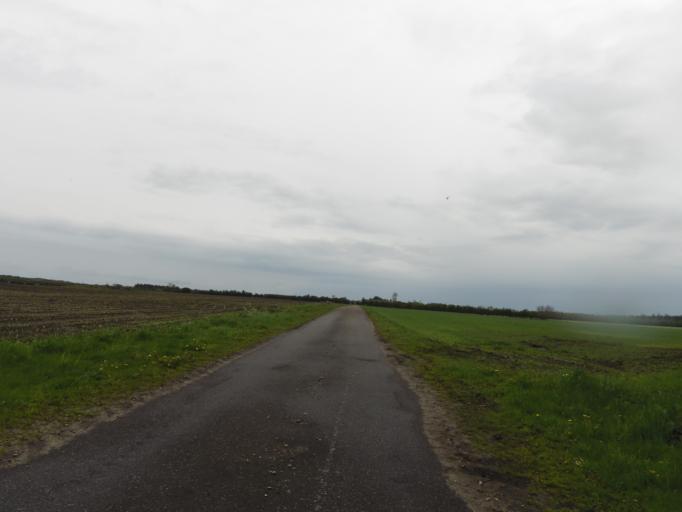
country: DK
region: South Denmark
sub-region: Haderslev Kommune
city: Gram
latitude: 55.2132
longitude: 8.9219
